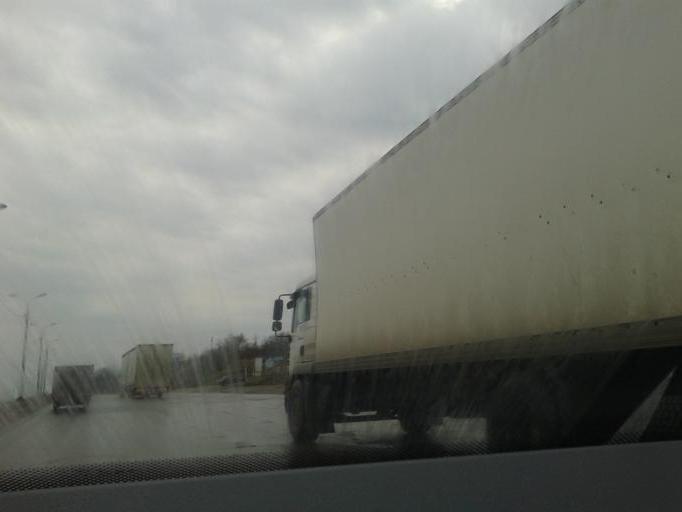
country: RU
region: Volgograd
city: Volgograd
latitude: 48.7298
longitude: 44.4508
